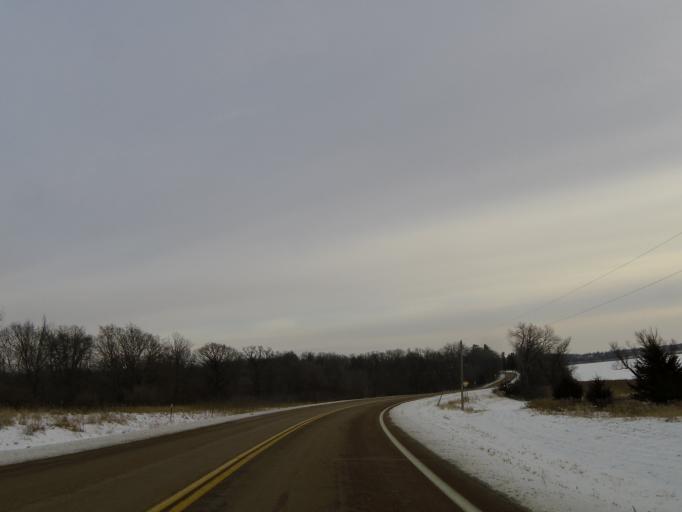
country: US
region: Minnesota
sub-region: Carver County
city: Victoria
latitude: 44.8719
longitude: -93.6807
